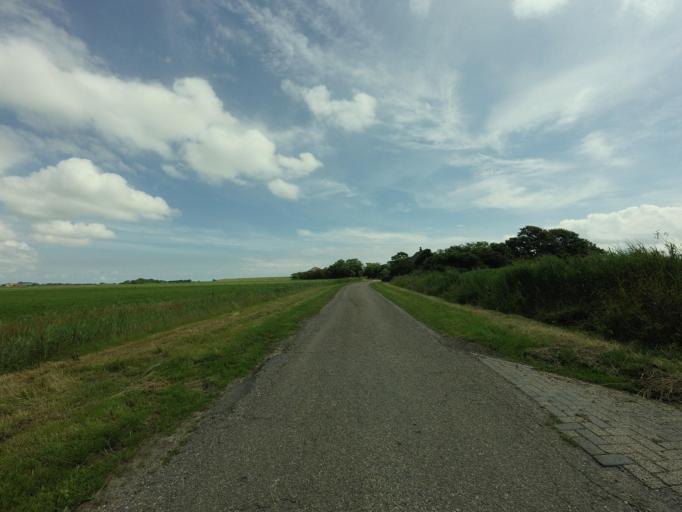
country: NL
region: North Holland
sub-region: Gemeente Texel
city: Den Burg
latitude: 53.0647
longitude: 4.8644
